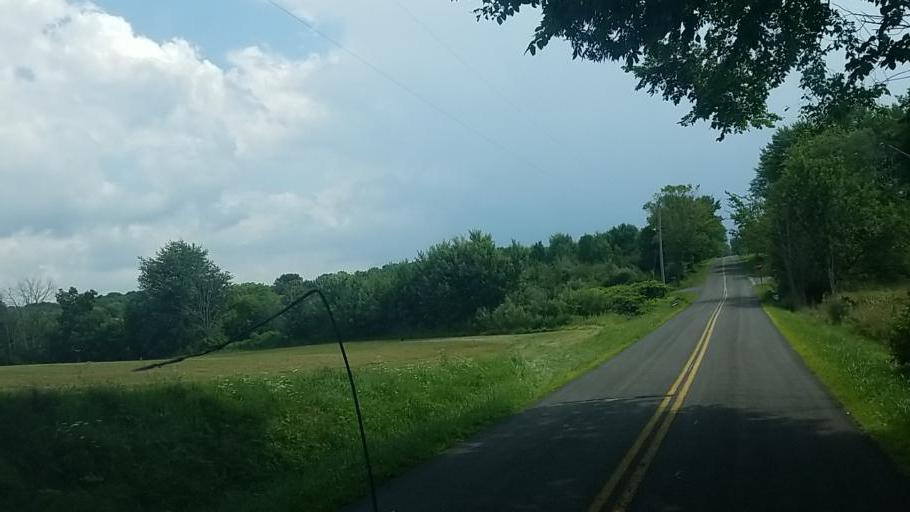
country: US
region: Ohio
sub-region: Medina County
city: Westfield Center
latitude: 41.1219
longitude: -81.9625
